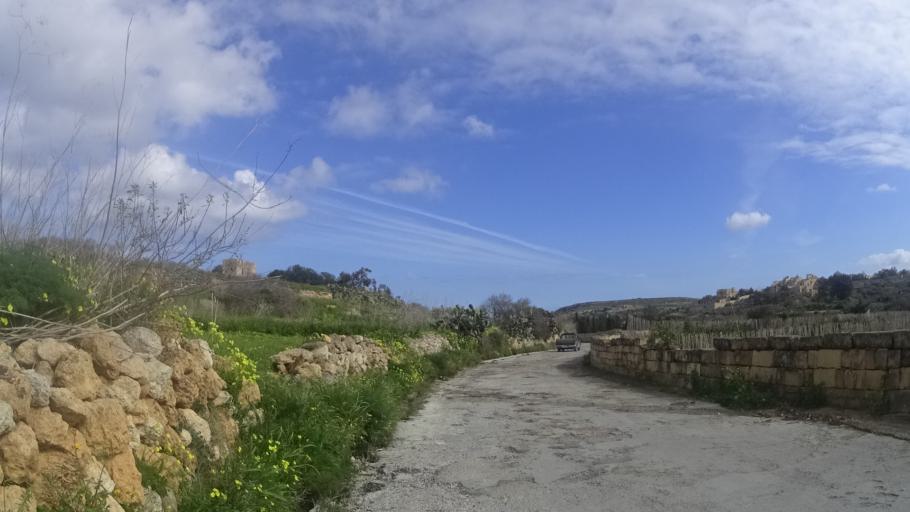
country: MT
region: In-Nadur
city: Nadur
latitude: 36.0442
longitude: 14.3022
